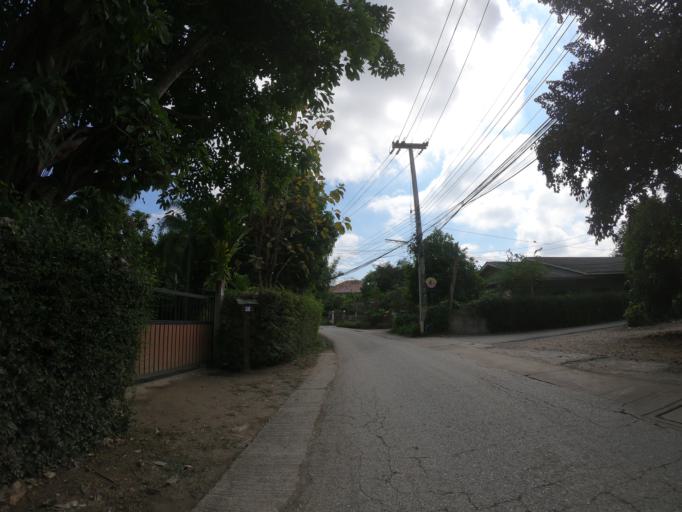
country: TH
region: Chiang Mai
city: San Sai
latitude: 18.8201
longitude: 99.0580
